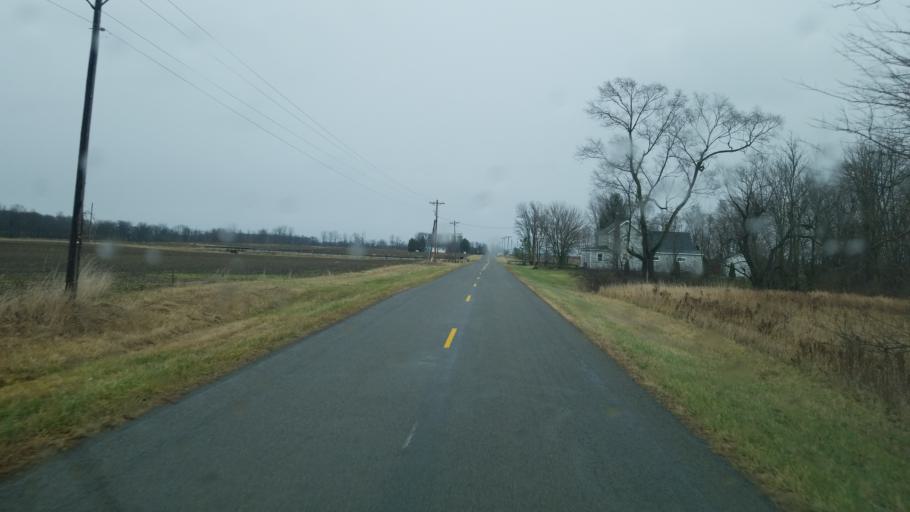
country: US
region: Ohio
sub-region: Logan County
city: Northwood
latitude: 40.4519
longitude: -83.5684
